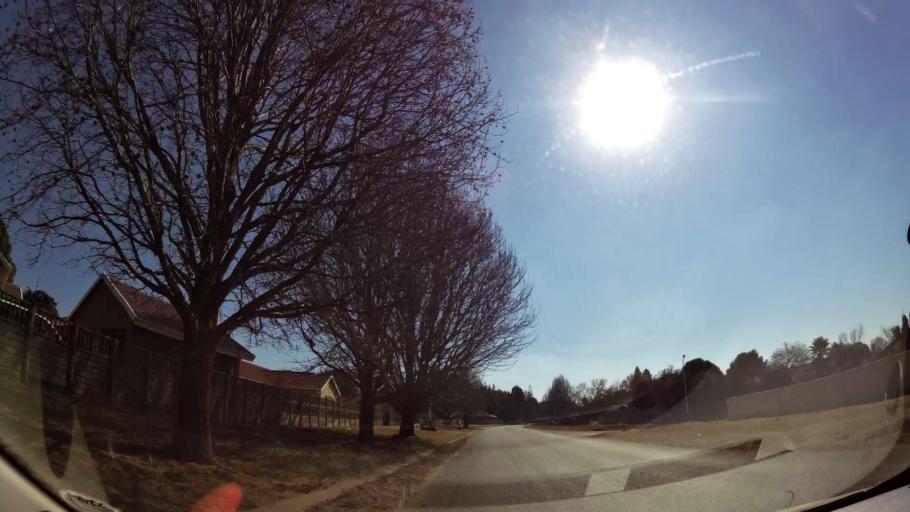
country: ZA
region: Mpumalanga
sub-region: Nkangala District Municipality
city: Witbank
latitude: -25.8327
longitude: 29.2430
